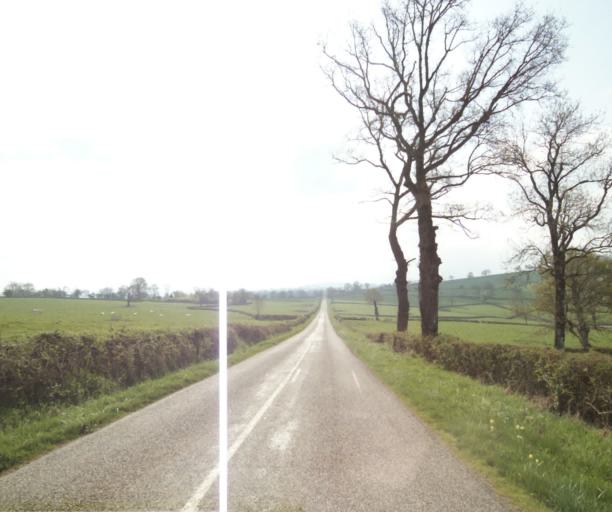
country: FR
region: Bourgogne
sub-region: Departement de Saone-et-Loire
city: Charolles
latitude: 46.3902
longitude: 4.2386
